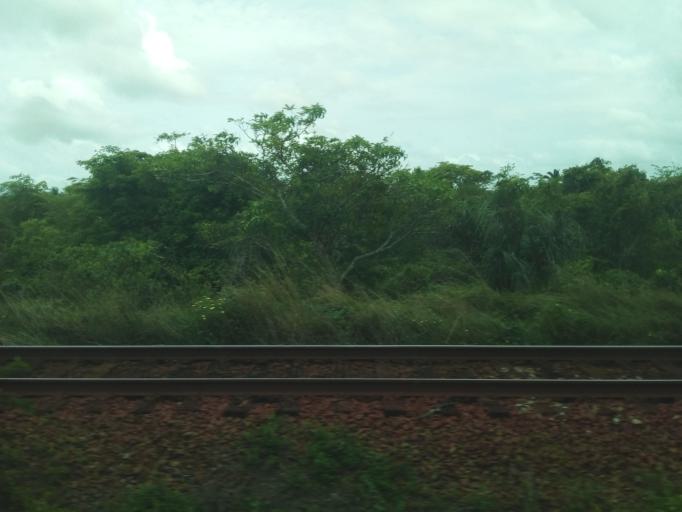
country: BR
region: Maranhao
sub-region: Arari
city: Arari
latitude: -3.5752
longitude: -44.7411
